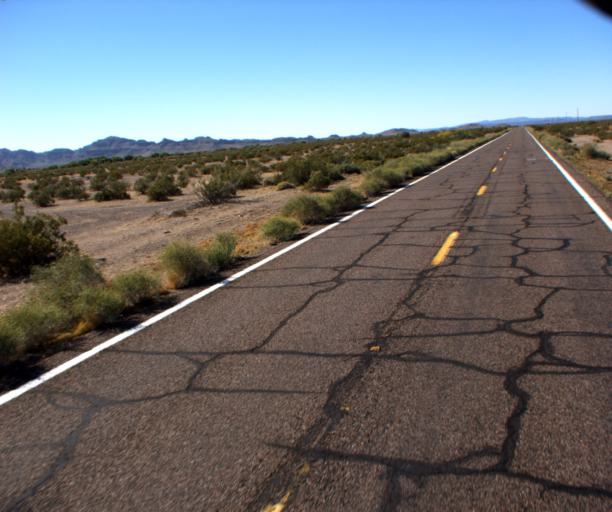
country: US
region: Arizona
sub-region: Maricopa County
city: Gila Bend
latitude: 32.7443
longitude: -112.8292
